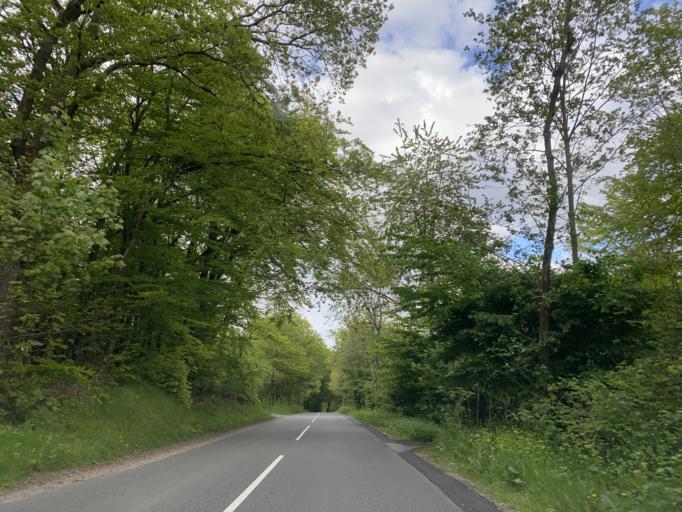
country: DK
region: Central Jutland
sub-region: Horsens Kommune
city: Braedstrup
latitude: 56.0271
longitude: 9.6511
